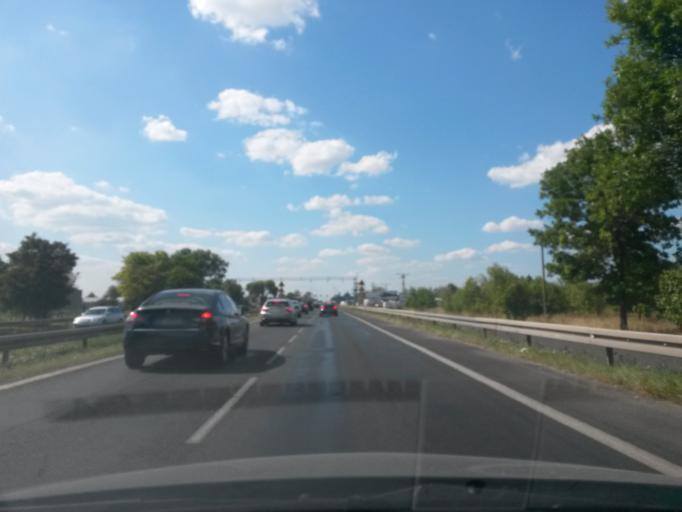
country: PL
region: Masovian Voivodeship
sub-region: Powiat warszawski zachodni
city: Dziekanow Lesny
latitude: 52.3568
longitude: 20.8380
